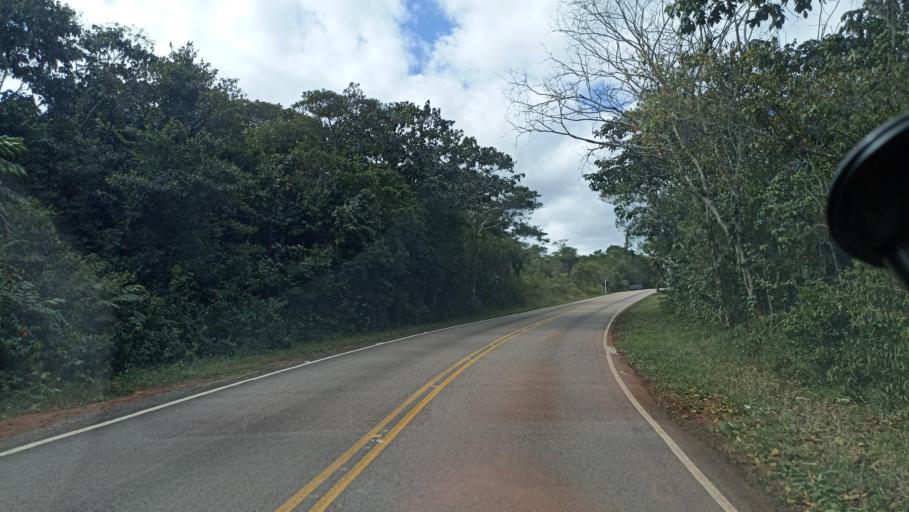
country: BR
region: Bahia
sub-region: Andarai
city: Vera Cruz
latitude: -12.9349
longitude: -41.2989
